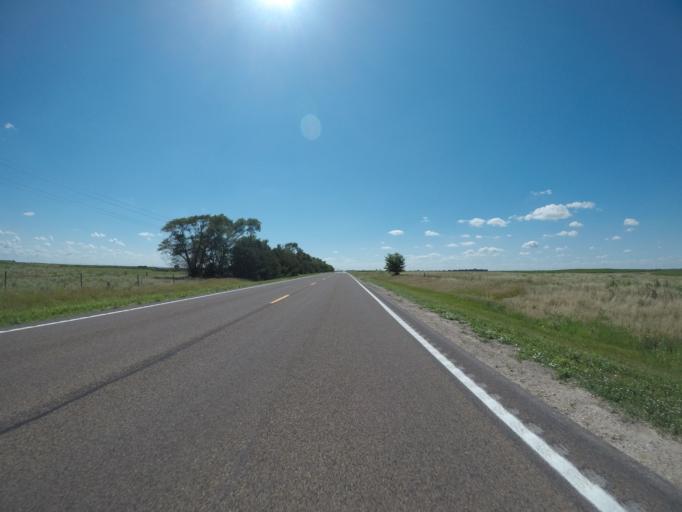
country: US
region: Nebraska
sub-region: Chase County
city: Imperial
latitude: 40.5376
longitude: -101.7301
